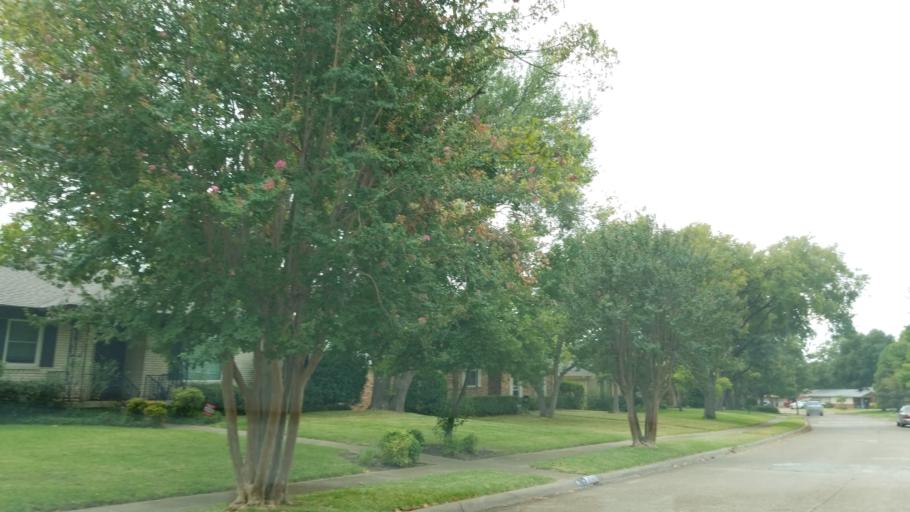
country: US
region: Texas
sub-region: Dallas County
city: Richardson
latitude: 32.9342
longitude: -96.7719
